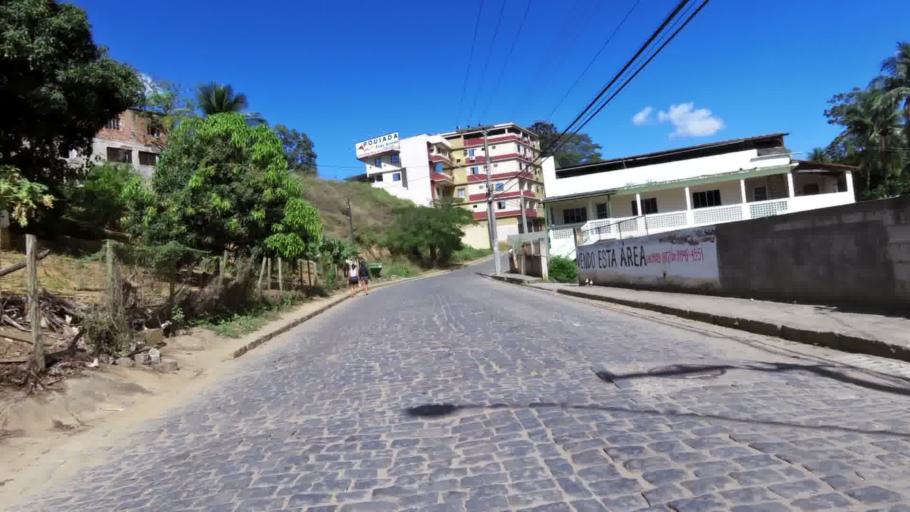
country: BR
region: Espirito Santo
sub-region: Rio Novo Do Sul
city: Rio Novo do Sul
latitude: -20.8652
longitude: -40.9365
